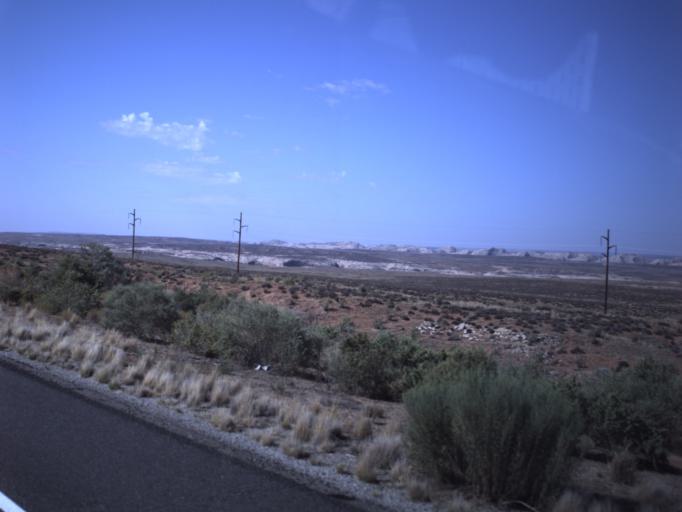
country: US
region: Utah
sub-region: San Juan County
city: Blanding
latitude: 37.3562
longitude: -109.5169
